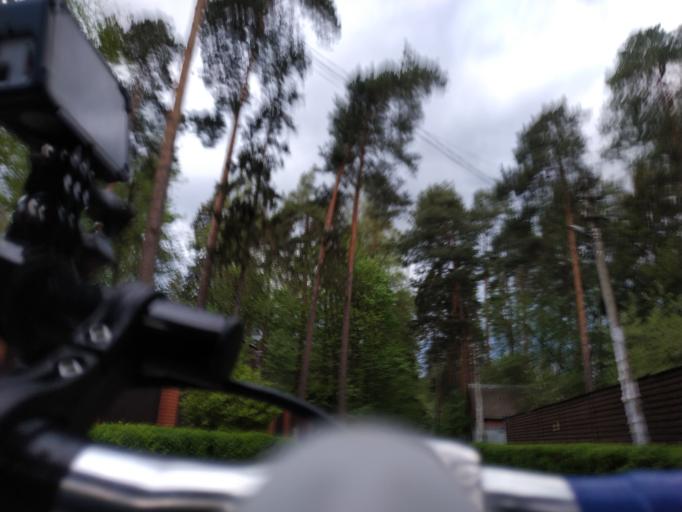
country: RU
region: Moskovskaya
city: Kratovo
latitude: 55.6014
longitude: 38.1770
